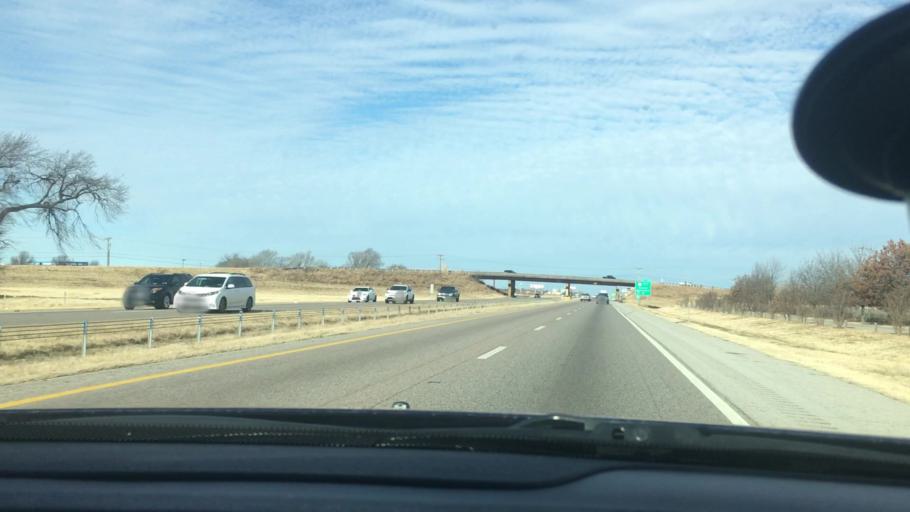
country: US
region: Oklahoma
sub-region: McClain County
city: Goldsby
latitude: 35.1512
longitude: -97.4748
